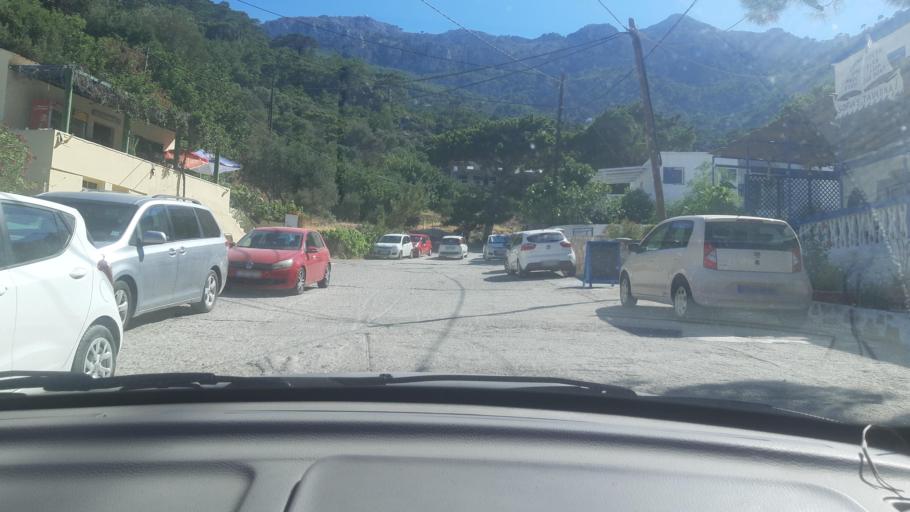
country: GR
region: South Aegean
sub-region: Nomos Dodekanisou
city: Karpathos
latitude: 35.5867
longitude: 27.1771
